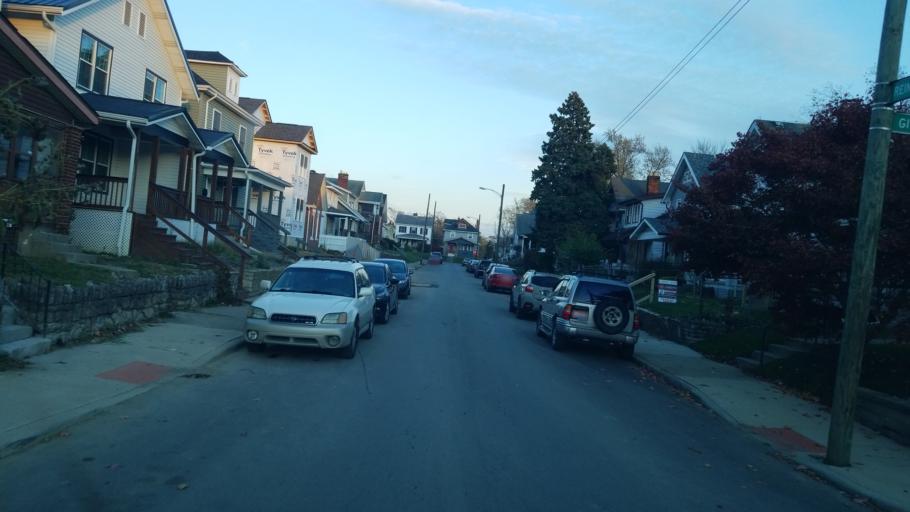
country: US
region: Ohio
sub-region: Franklin County
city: Columbus
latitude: 39.9430
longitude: -82.9750
